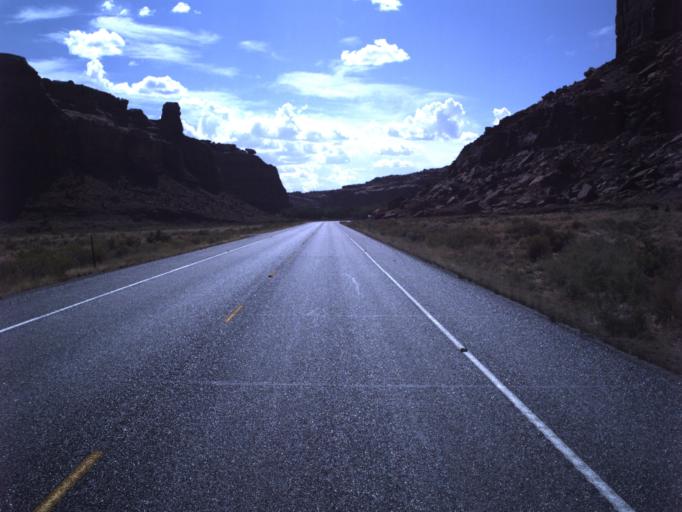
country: US
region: Utah
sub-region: Grand County
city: Moab
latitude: 38.6604
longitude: -109.7062
